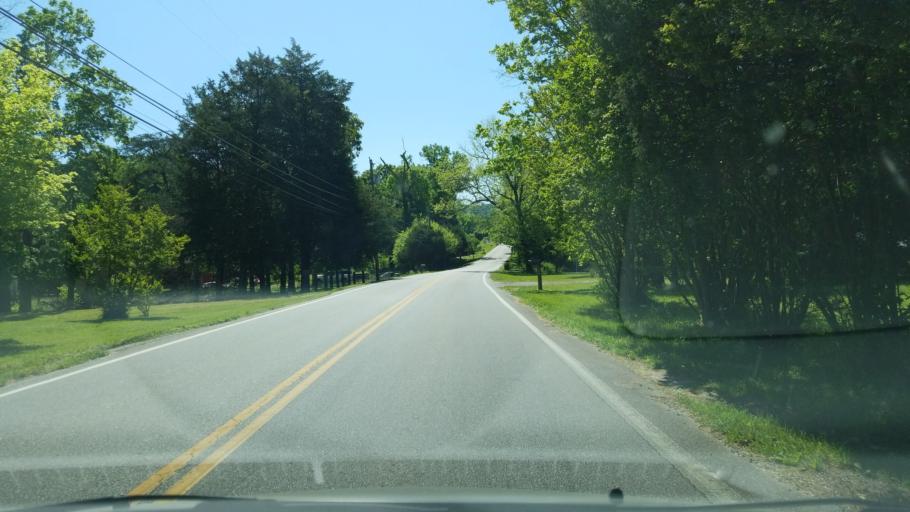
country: US
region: Tennessee
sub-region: Hamilton County
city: Middle Valley
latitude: 35.1853
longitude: -85.1862
